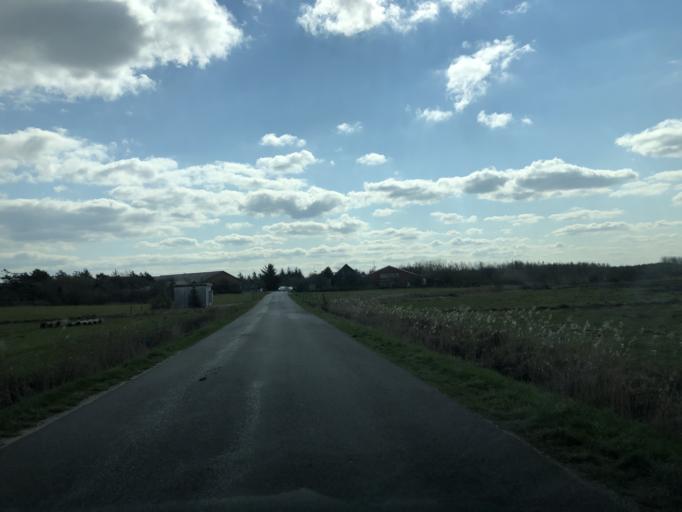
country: DK
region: Central Jutland
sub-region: Holstebro Kommune
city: Ulfborg
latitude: 56.3965
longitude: 8.2227
